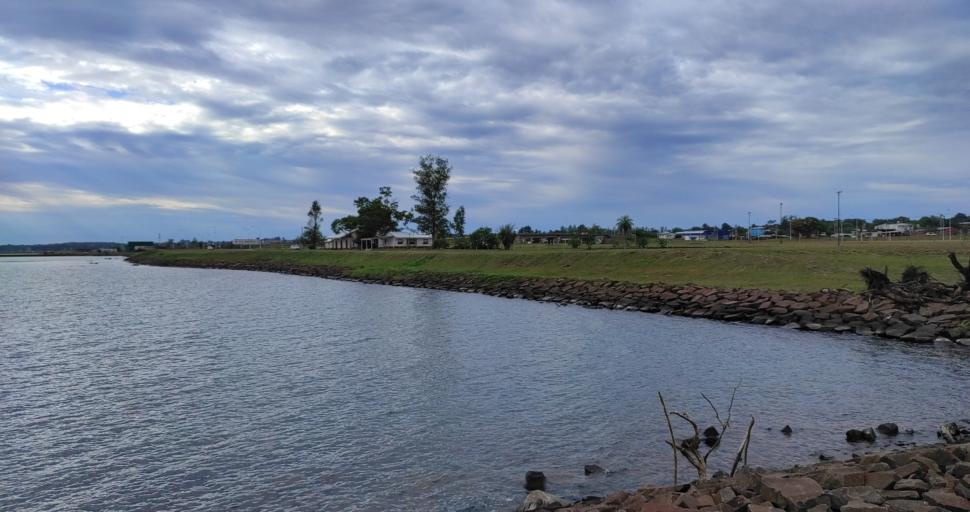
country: AR
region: Misiones
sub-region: Departamento de Capital
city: Posadas
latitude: -27.4203
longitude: -55.8752
